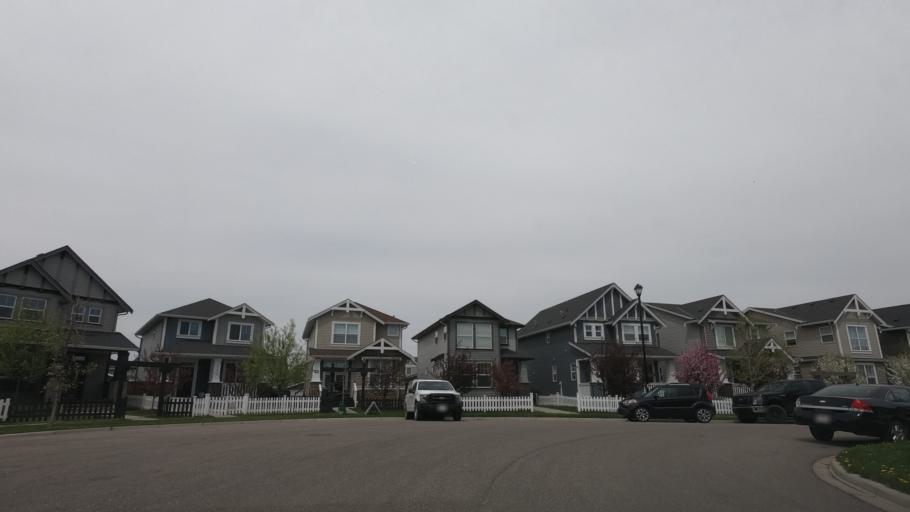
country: CA
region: Alberta
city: Airdrie
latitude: 51.3020
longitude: -114.0362
